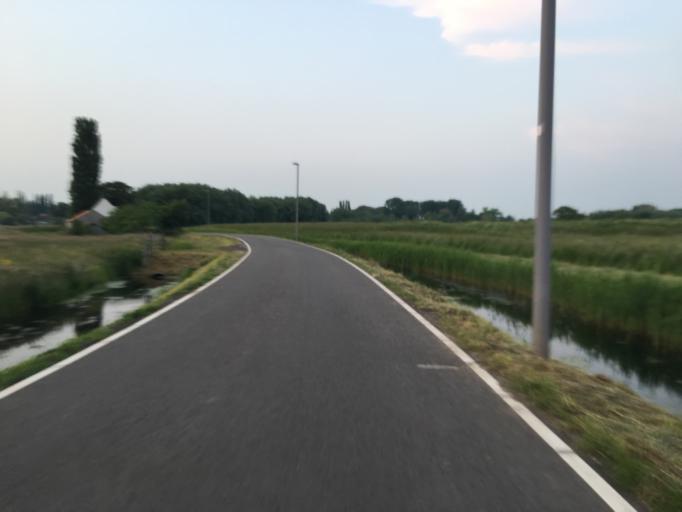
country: NL
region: South Holland
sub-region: Gemeente Schiedam
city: Schiedam
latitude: 51.9526
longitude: 4.3952
